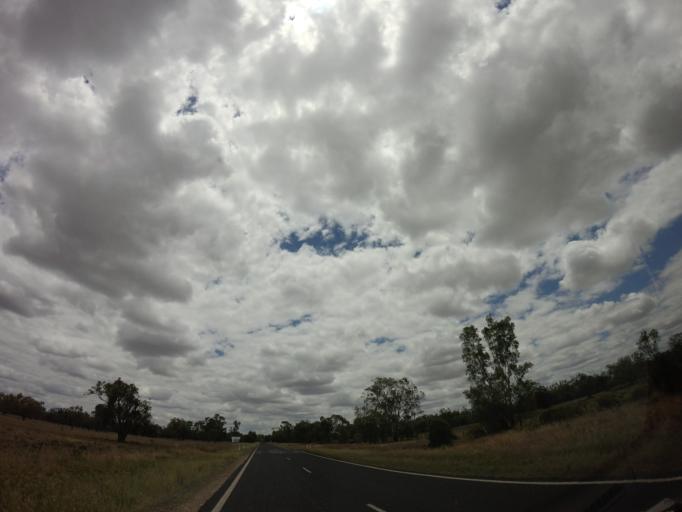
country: AU
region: Queensland
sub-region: Goondiwindi
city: Goondiwindi
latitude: -28.4716
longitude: 150.2926
